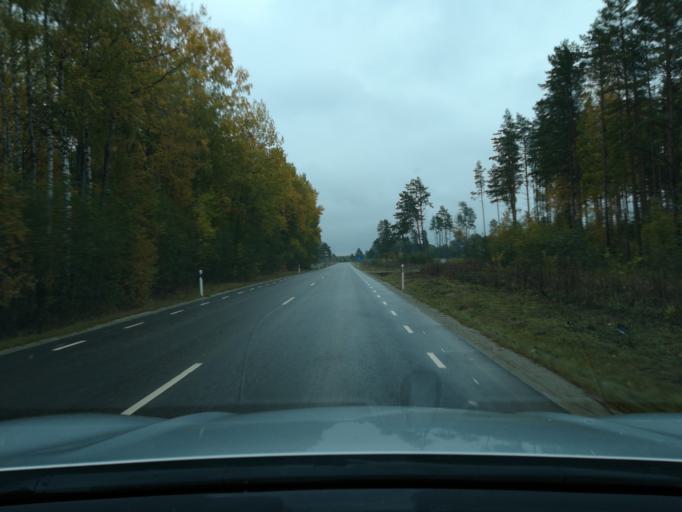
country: EE
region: Ida-Virumaa
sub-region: Johvi vald
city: Johvi
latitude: 59.2969
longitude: 27.4839
